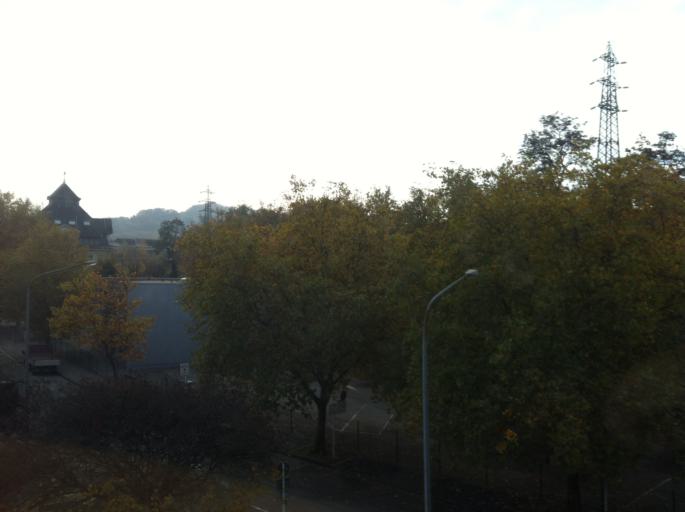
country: LU
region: Luxembourg
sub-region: Canton d'Esch-sur-Alzette
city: Esch-sur-Alzette
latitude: 49.4912
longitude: 5.9751
